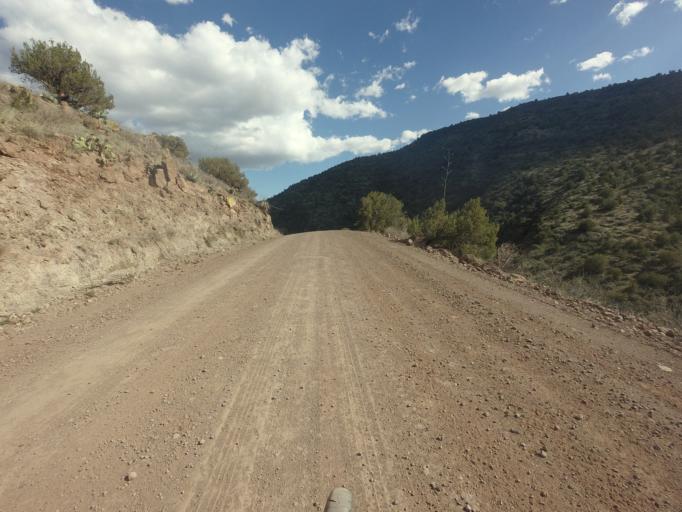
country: US
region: Arizona
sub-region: Yavapai County
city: Camp Verde
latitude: 34.4543
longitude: -111.7030
